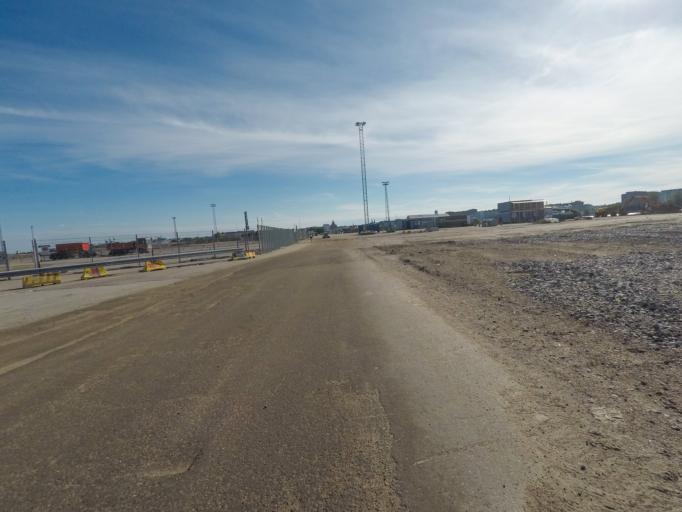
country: FI
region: Uusimaa
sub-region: Helsinki
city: Helsinki
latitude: 60.1802
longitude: 24.9746
